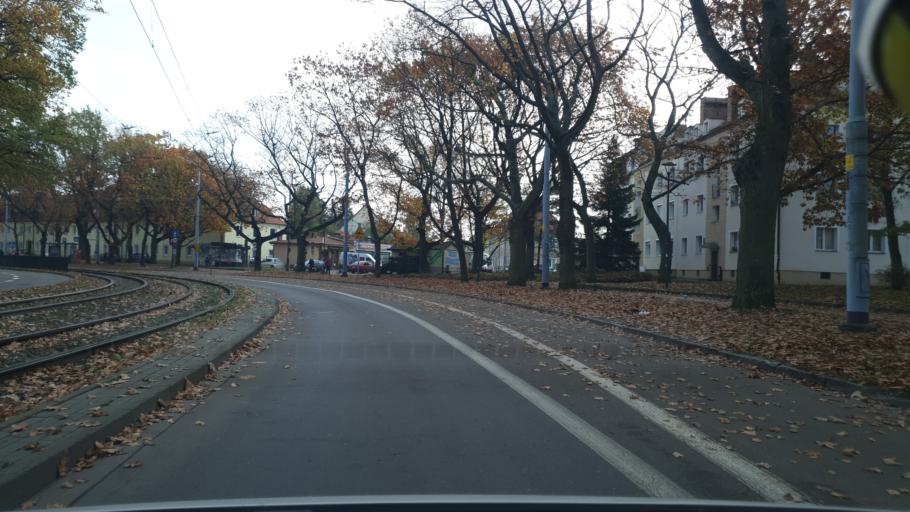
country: PL
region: Pomeranian Voivodeship
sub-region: Sopot
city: Sopot
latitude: 54.3871
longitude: 18.5834
